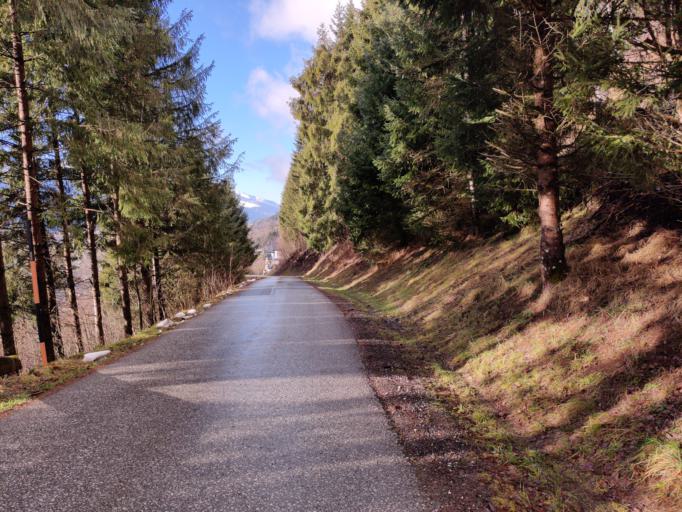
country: AT
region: Salzburg
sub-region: Politischer Bezirk Zell am See
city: Zell am See
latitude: 47.2974
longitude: 12.7801
